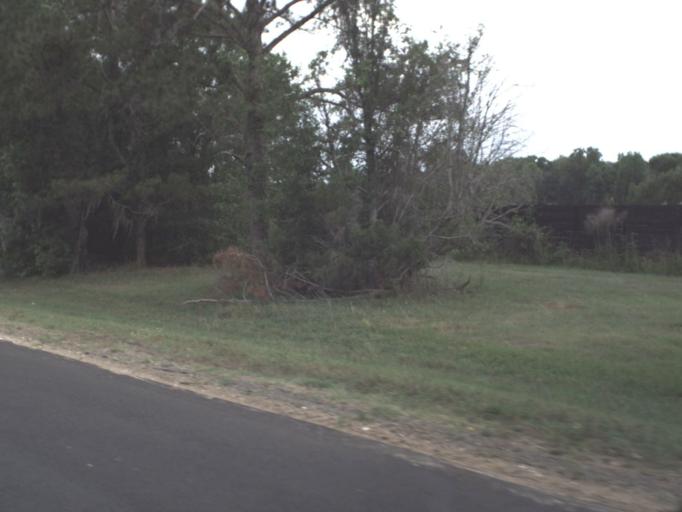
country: US
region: Florida
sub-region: Marion County
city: Citra
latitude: 29.3589
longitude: -82.2229
